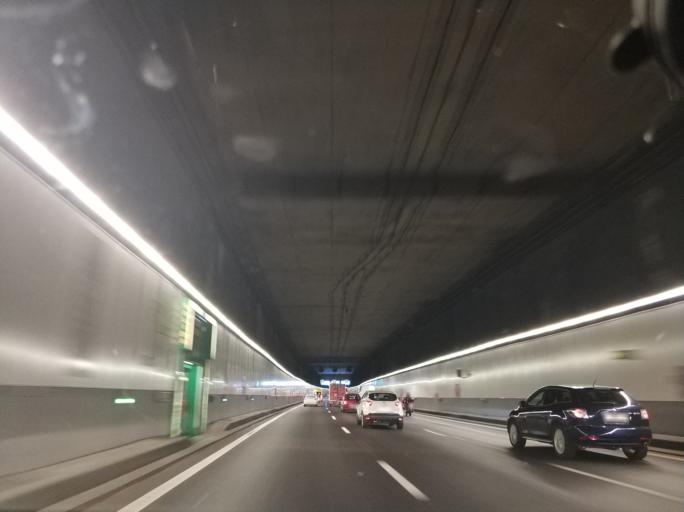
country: ES
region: Madrid
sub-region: Provincia de Madrid
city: Usera
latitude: 40.3898
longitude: -3.6985
